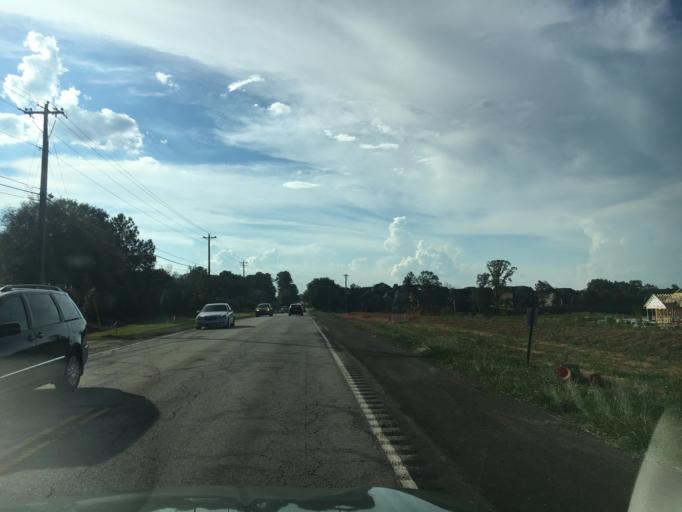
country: US
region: South Carolina
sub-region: Greenville County
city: Five Forks
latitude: 34.8013
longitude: -82.2068
